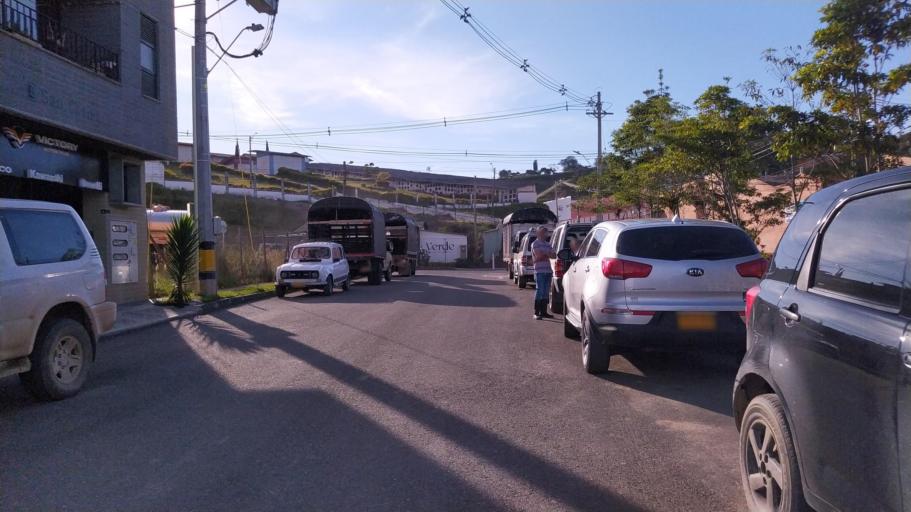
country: CO
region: Antioquia
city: Entrerrios
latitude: 6.5682
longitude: -75.5188
